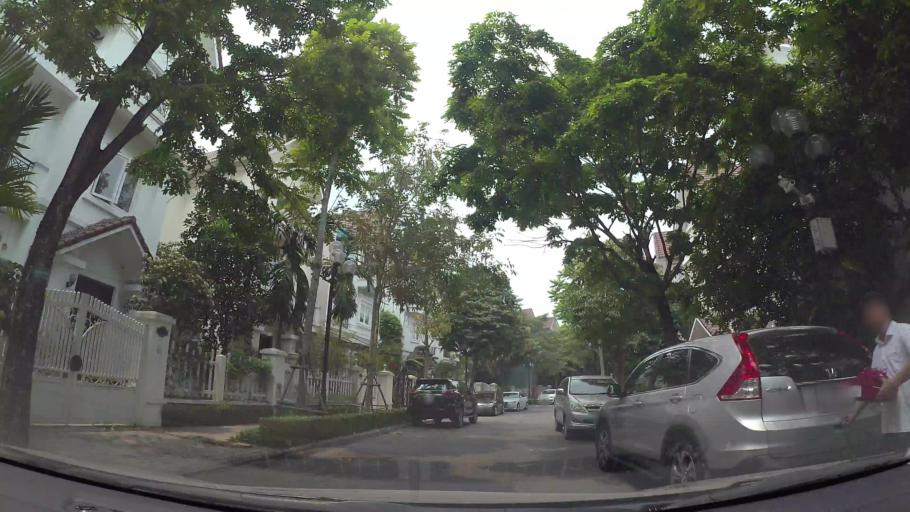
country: VN
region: Ha Noi
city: Trau Quy
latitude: 21.0457
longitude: 105.9156
